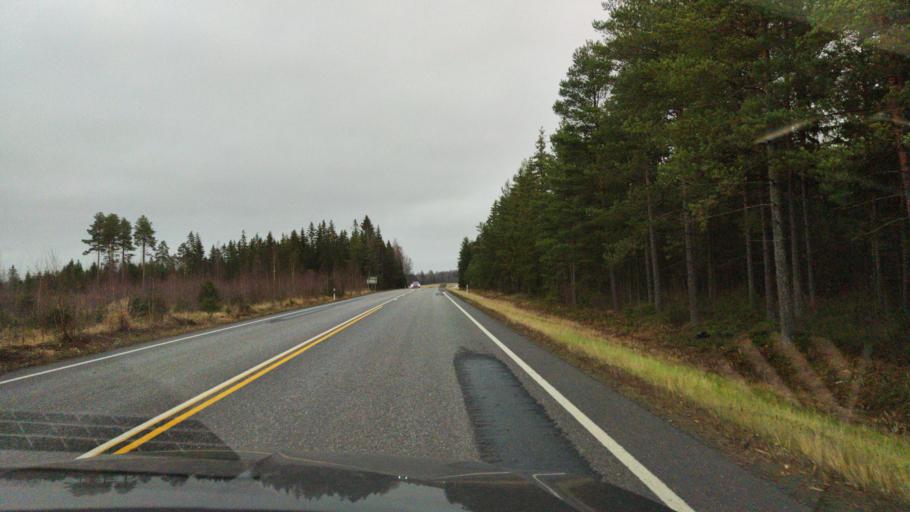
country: FI
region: Satakunta
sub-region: Rauma
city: Kiukainen
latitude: 61.2530
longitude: 22.0706
